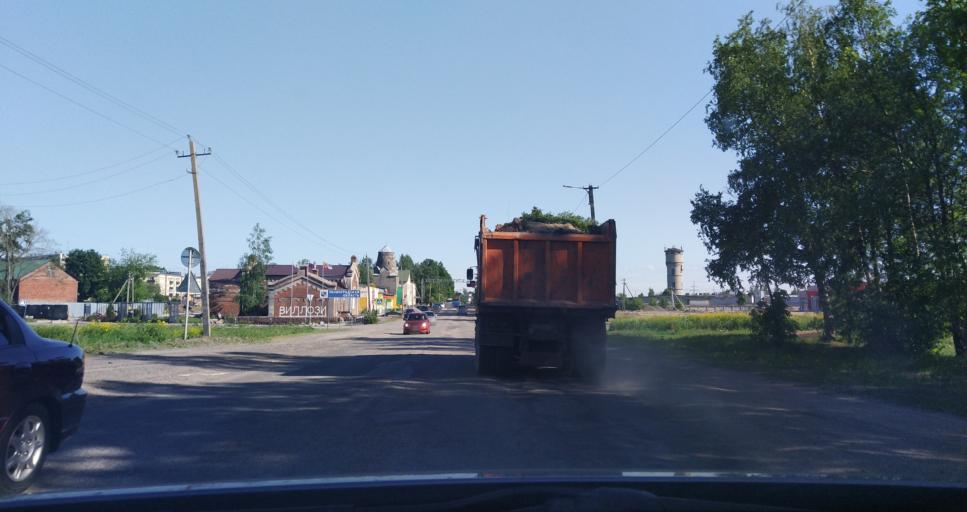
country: RU
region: Leningrad
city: Taytsy
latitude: 59.6997
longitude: 30.1004
